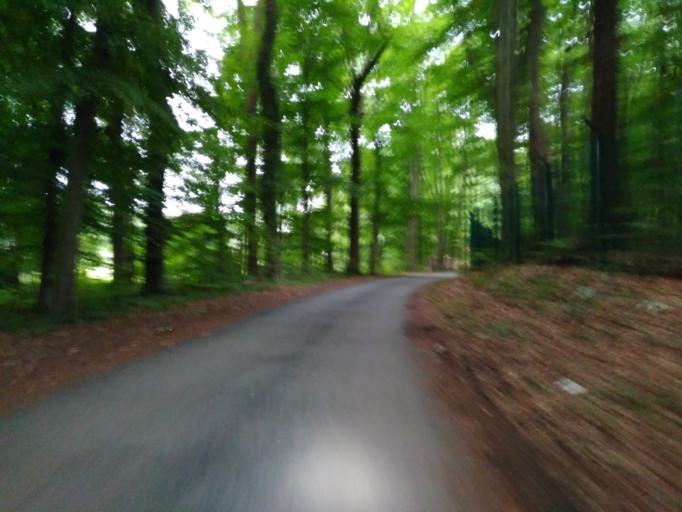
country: DE
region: North Rhine-Westphalia
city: Dorsten
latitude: 51.6226
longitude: 6.9774
